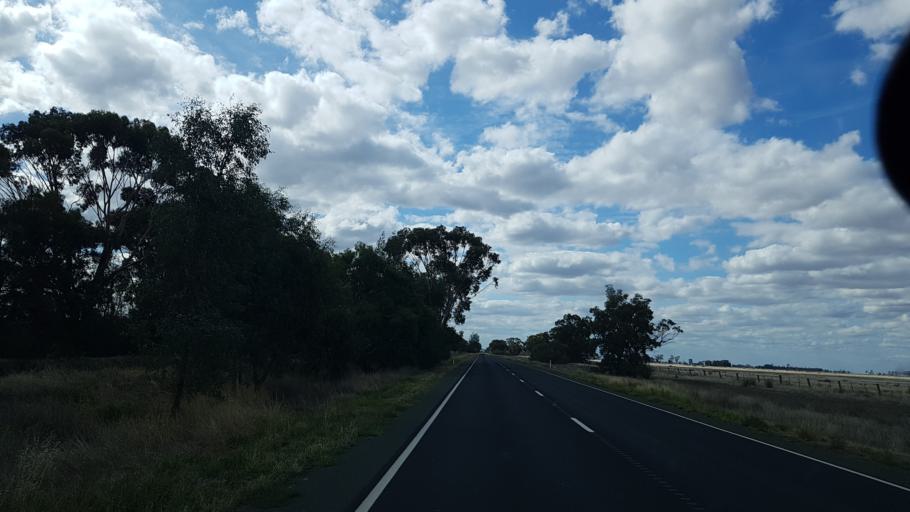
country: AU
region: Victoria
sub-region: Swan Hill
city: Swan Hill
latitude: -35.9863
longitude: 143.9457
